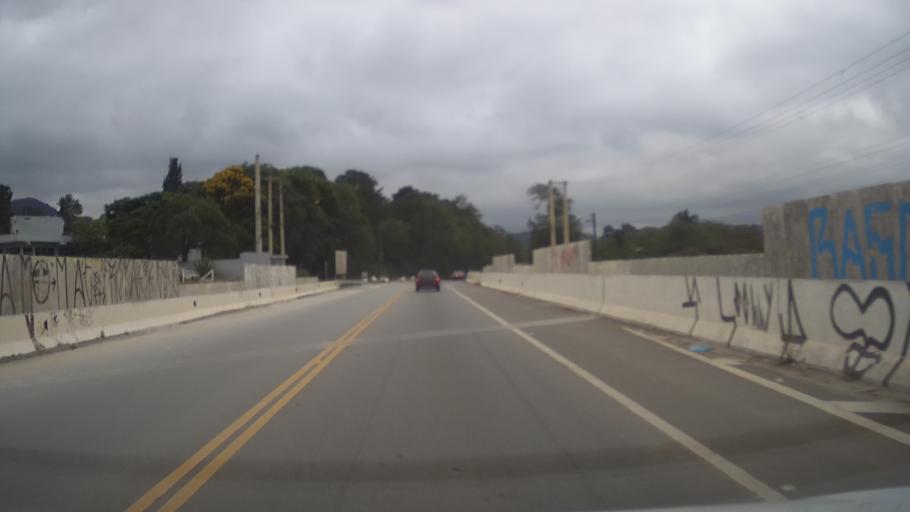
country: BR
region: Sao Paulo
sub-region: Guarulhos
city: Guarulhos
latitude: -23.3890
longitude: -46.4424
